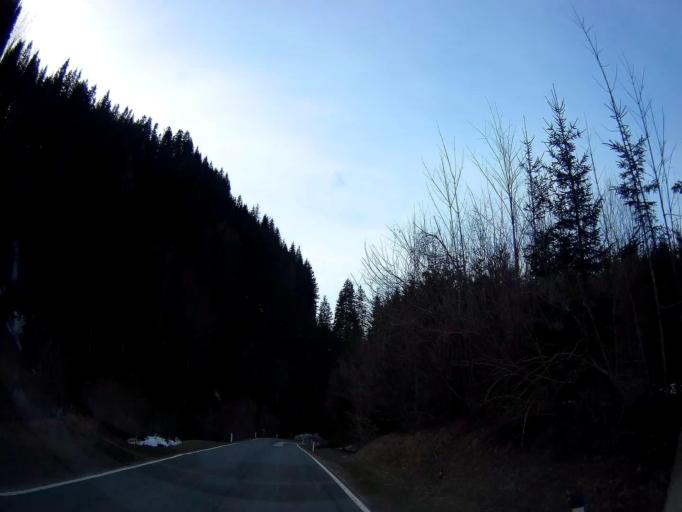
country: AT
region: Salzburg
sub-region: Politischer Bezirk Hallein
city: Abtenau
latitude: 47.5378
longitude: 13.4223
